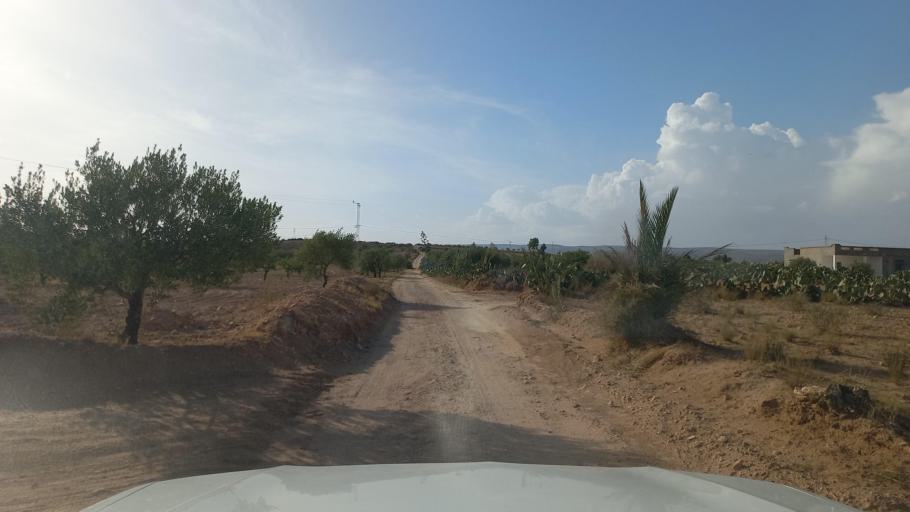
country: TN
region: Al Qasrayn
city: Kasserine
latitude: 35.2326
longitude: 8.9217
